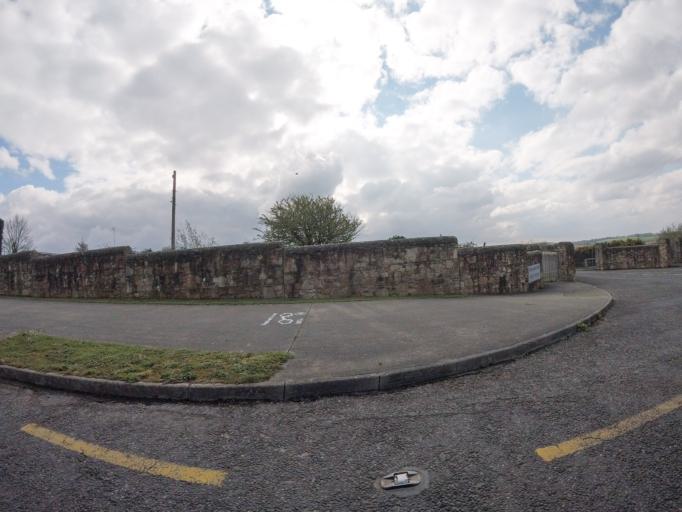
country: IE
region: Munster
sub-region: Waterford
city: Waterford
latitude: 52.2370
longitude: -7.0960
